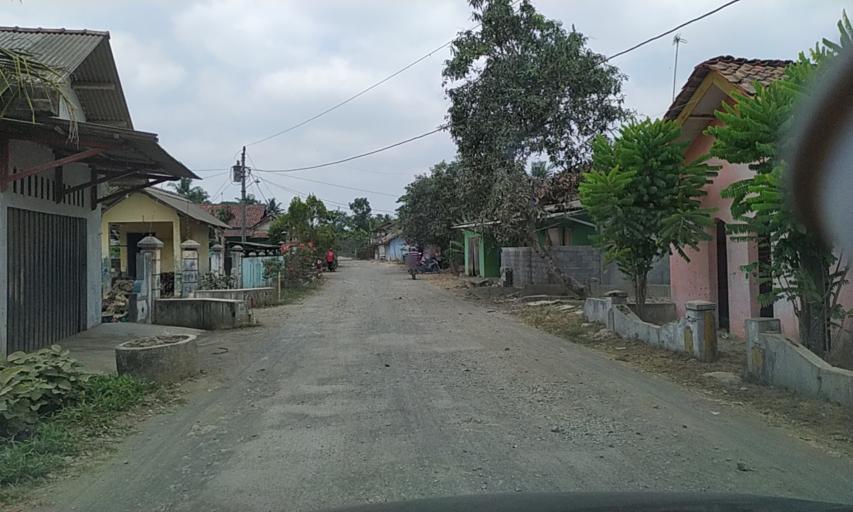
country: ID
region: Central Java
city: Sidakaya
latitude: -7.5725
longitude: 108.8643
